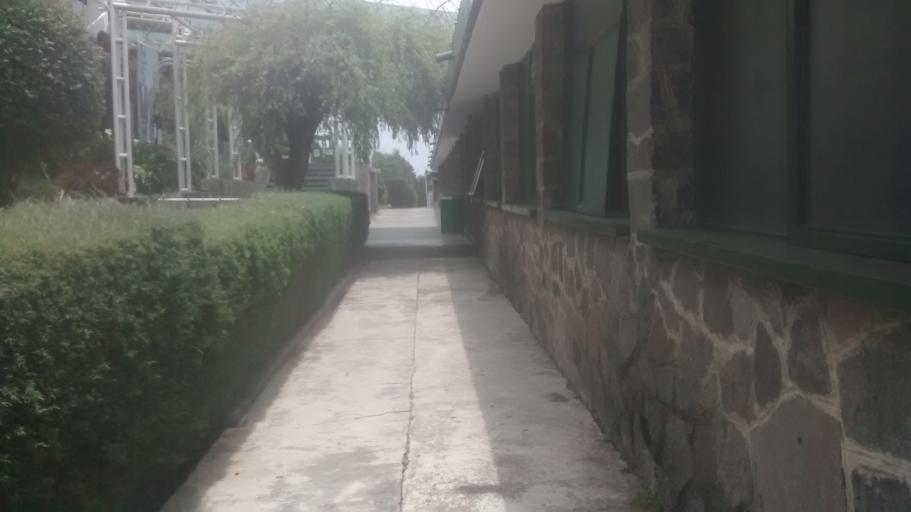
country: MX
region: Mexico
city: San Buenaventura
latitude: 19.2820
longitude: -99.6787
